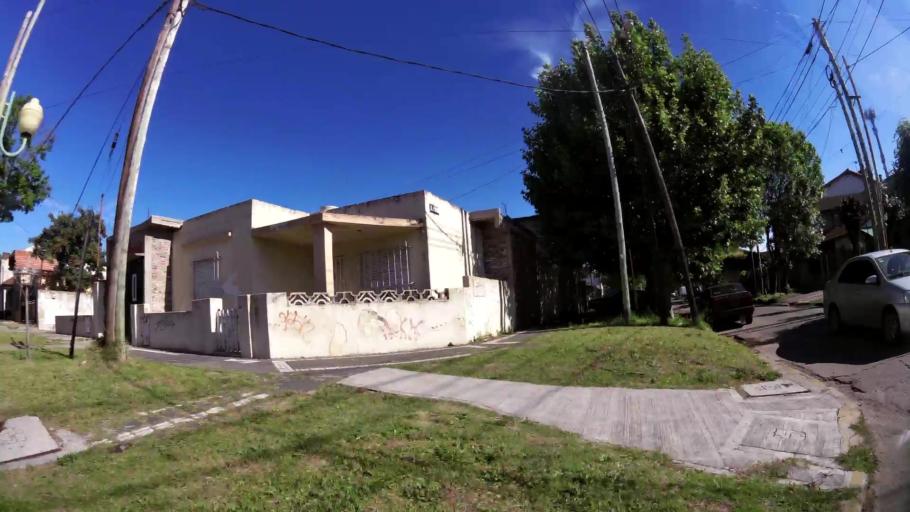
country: AR
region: Buenos Aires
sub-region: Partido de Lomas de Zamora
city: Lomas de Zamora
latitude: -34.7546
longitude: -58.4178
